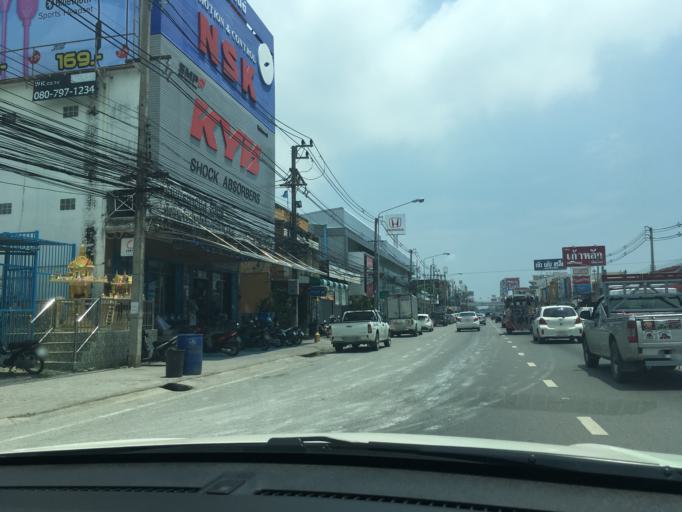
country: TH
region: Chon Buri
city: Chon Buri
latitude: 13.3483
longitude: 100.9793
